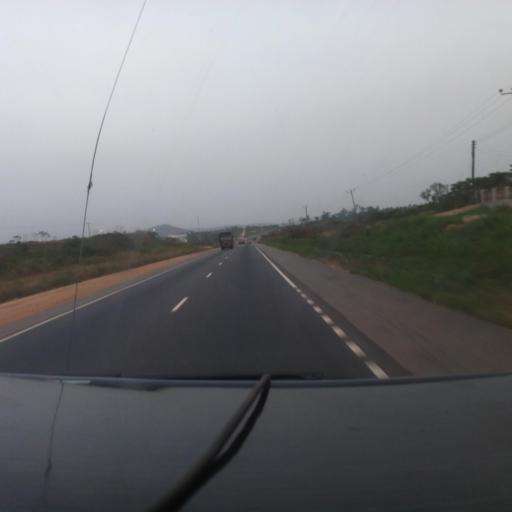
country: GH
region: Eastern
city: Nsawam
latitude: 5.8694
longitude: -0.3667
